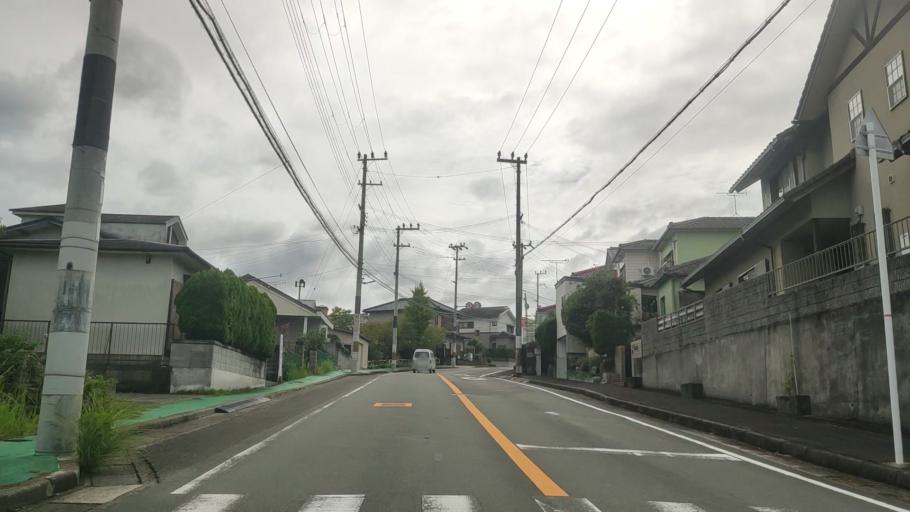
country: JP
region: Wakayama
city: Tanabe
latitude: 33.6765
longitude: 135.3756
